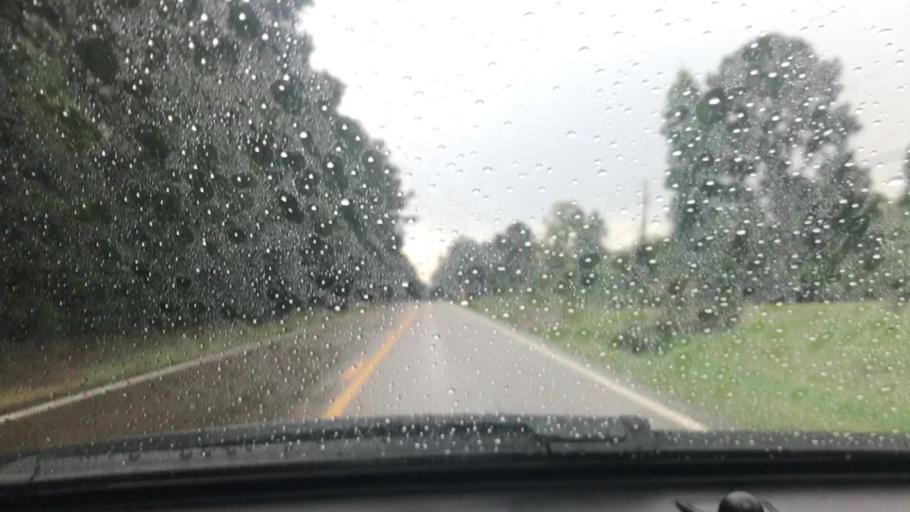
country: US
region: Mississippi
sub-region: Pike County
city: Summit
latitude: 31.2967
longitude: -90.5041
